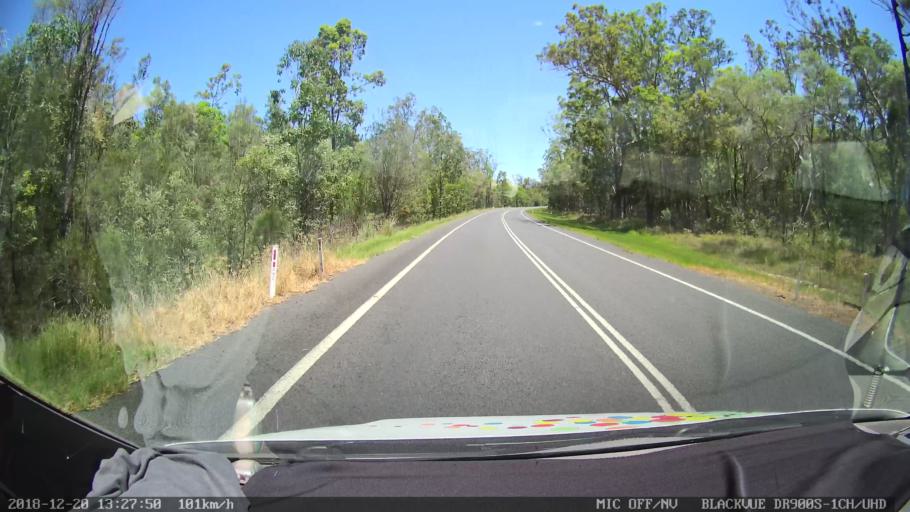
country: AU
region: New South Wales
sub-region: Clarence Valley
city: Gordon
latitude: -29.1658
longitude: 152.9931
